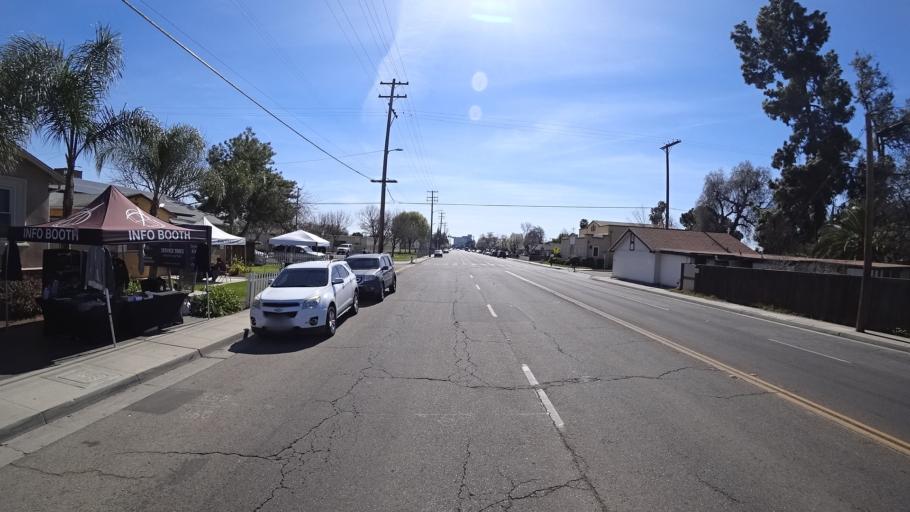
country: US
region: California
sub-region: Fresno County
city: Fresno
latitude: 36.7562
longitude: -119.8086
